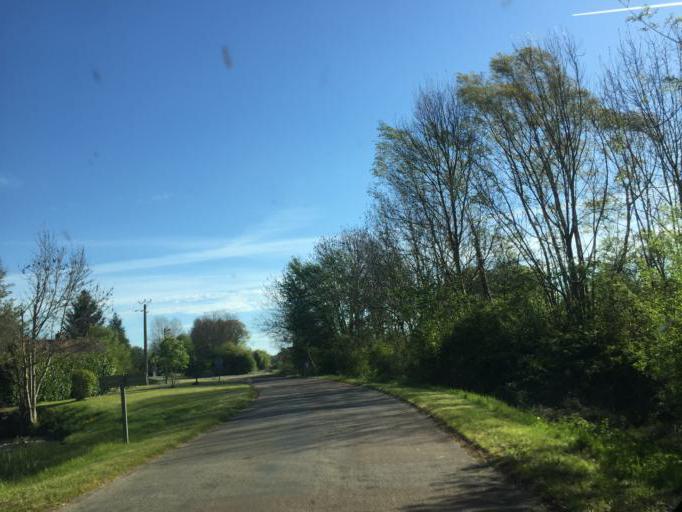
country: FR
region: Bourgogne
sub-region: Departement de la Nievre
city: Clamecy
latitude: 47.5044
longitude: 3.5149
